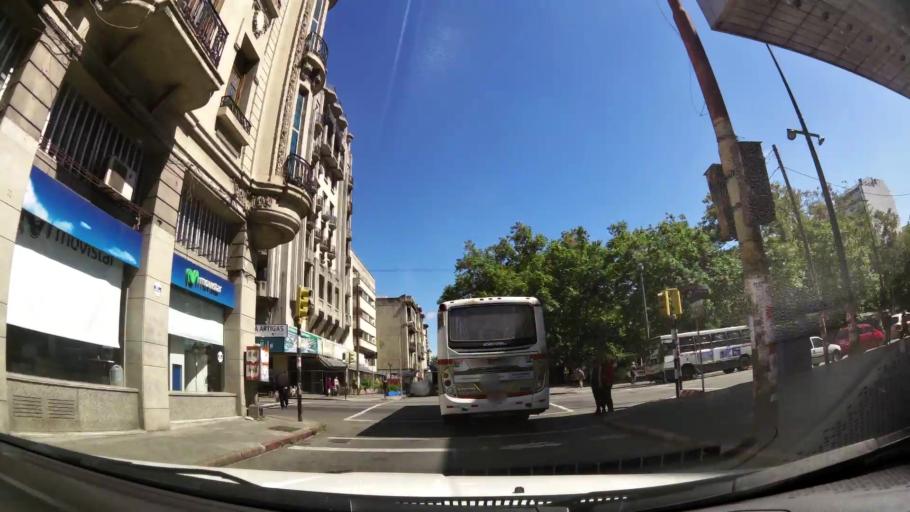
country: UY
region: Montevideo
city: Montevideo
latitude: -34.9039
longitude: -56.1804
